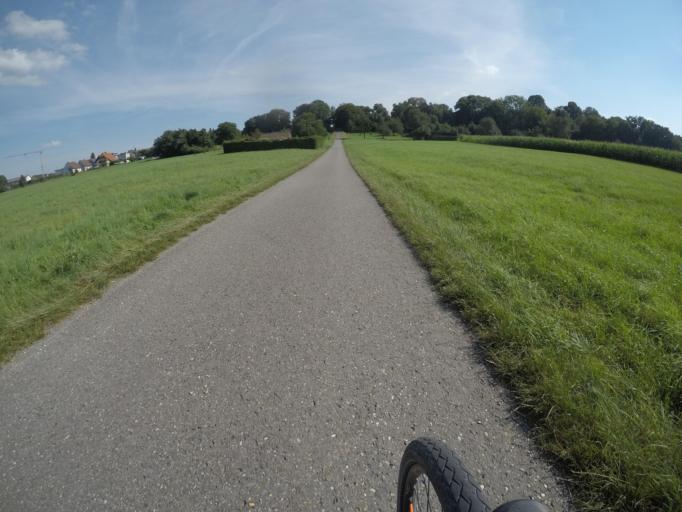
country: DE
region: Baden-Wuerttemberg
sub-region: Karlsruhe Region
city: Olbronn-Durrn
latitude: 48.9601
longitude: 8.7555
